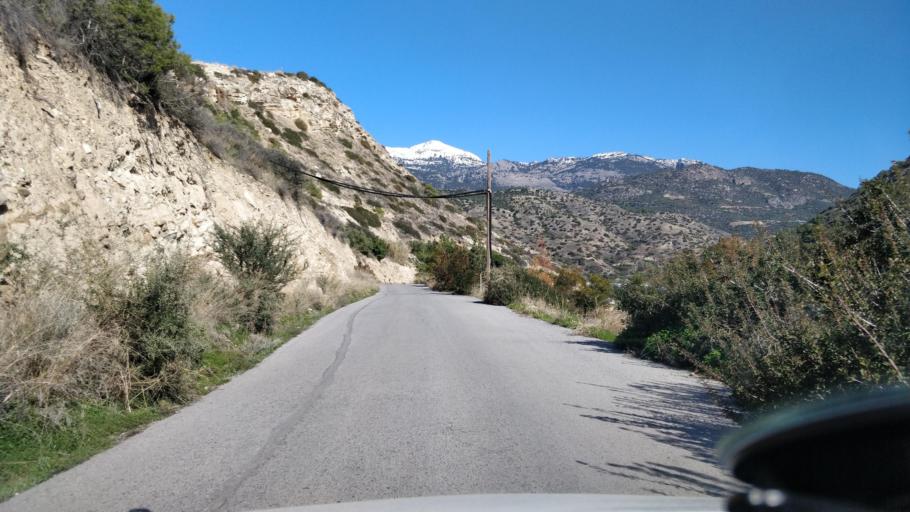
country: GR
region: Crete
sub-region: Nomos Lasithiou
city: Gra Liyia
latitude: 34.9884
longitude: 25.4813
